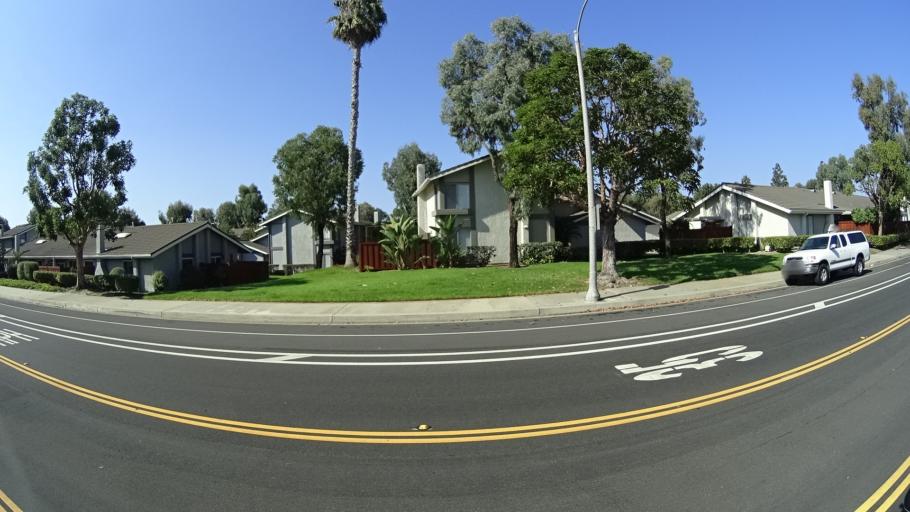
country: US
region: California
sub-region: Orange County
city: San Clemente
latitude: 33.4528
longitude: -117.6523
